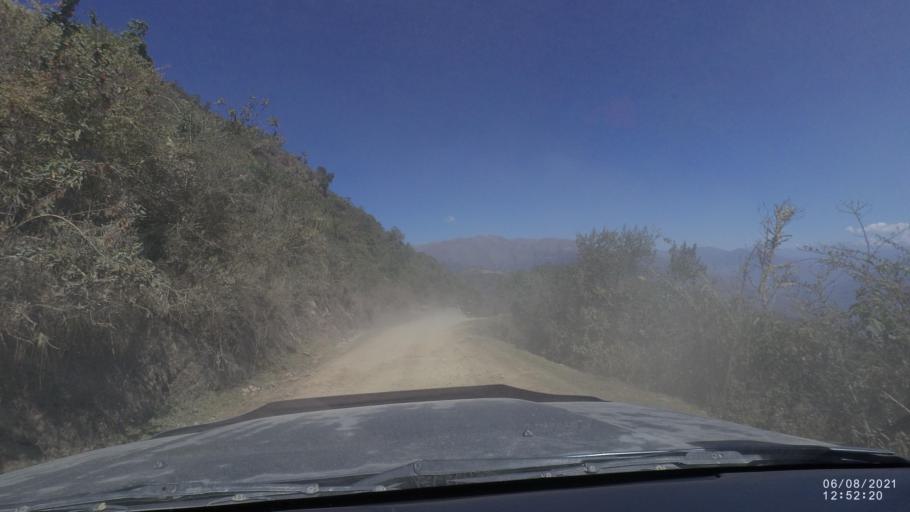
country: BO
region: Cochabamba
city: Colchani
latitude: -16.7639
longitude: -66.6828
